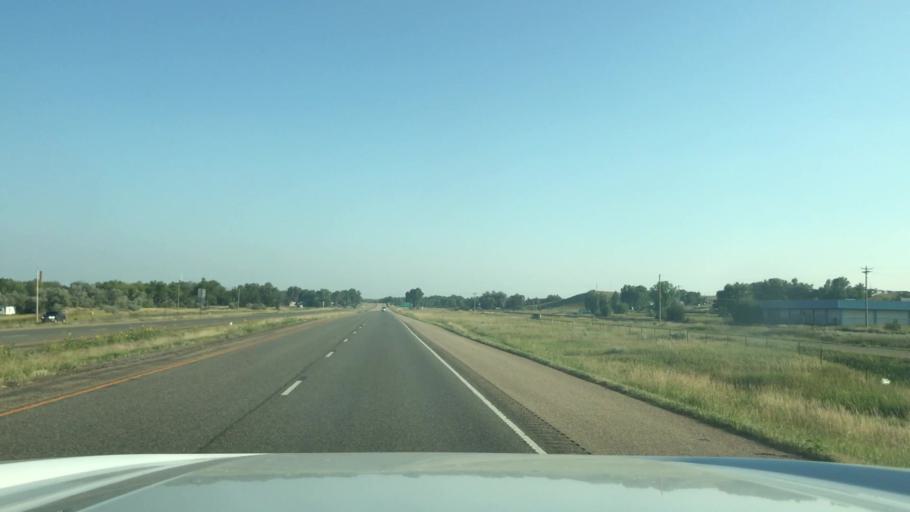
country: US
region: Montana
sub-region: Big Horn County
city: Crow Agency
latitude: 45.6120
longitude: -107.4646
